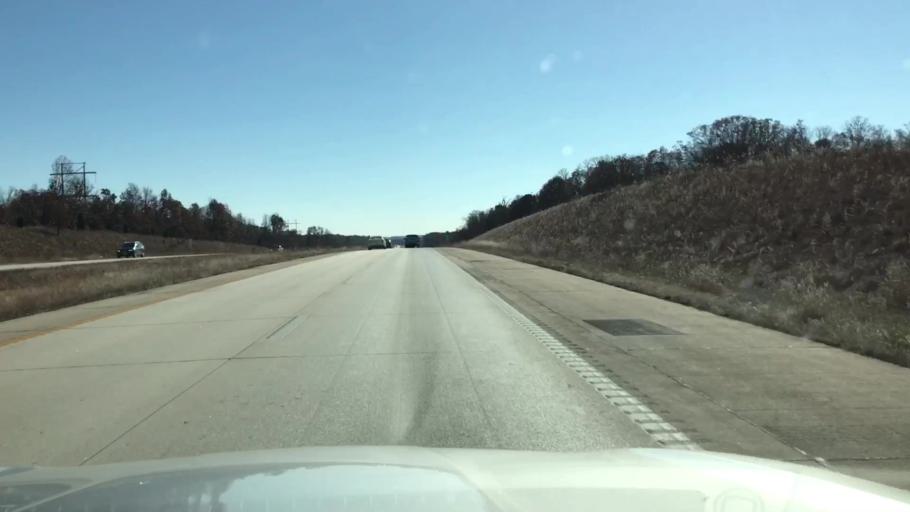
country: US
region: Missouri
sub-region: Jasper County
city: Duquesne
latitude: 37.0245
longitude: -94.4301
